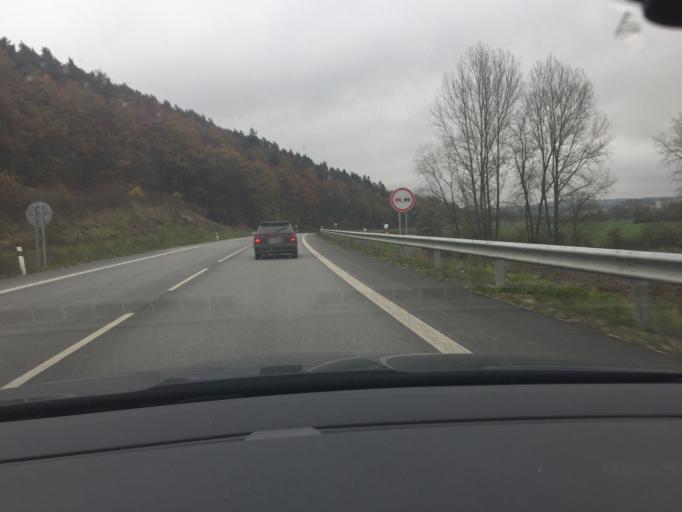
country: SK
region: Presovsky
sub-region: Okres Bardejov
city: Bardejov
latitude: 49.3059
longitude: 21.2270
